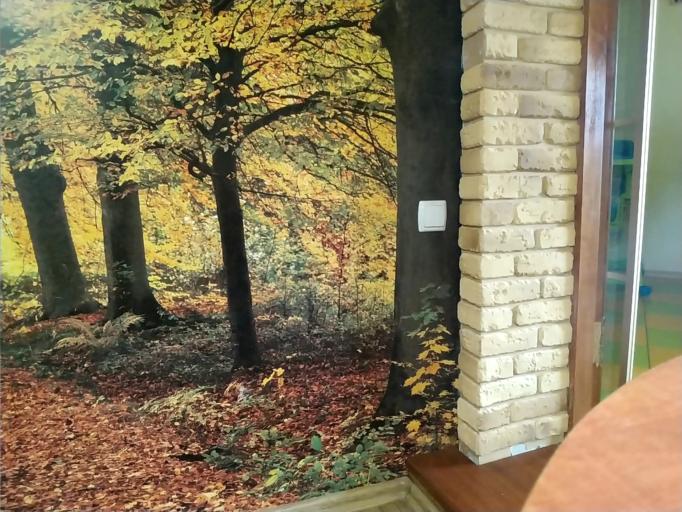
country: RU
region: Smolensk
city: Dorogobuzh
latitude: 54.8731
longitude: 33.3119
